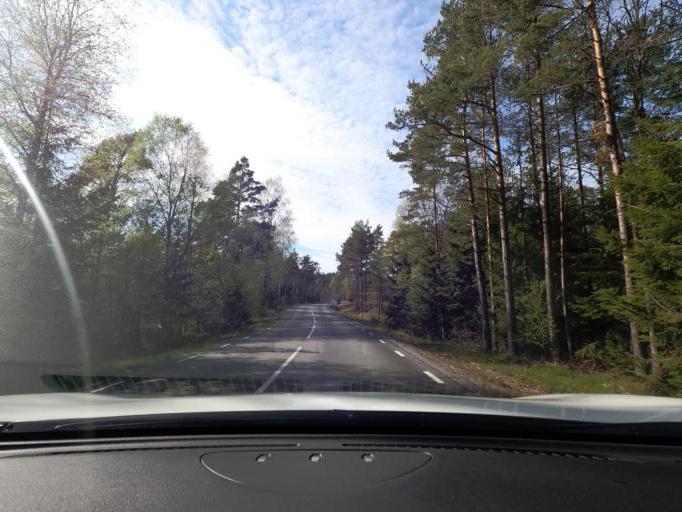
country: SE
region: Vaestra Goetaland
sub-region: Harryda Kommun
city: Landvetter
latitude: 57.6658
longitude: 12.2460
